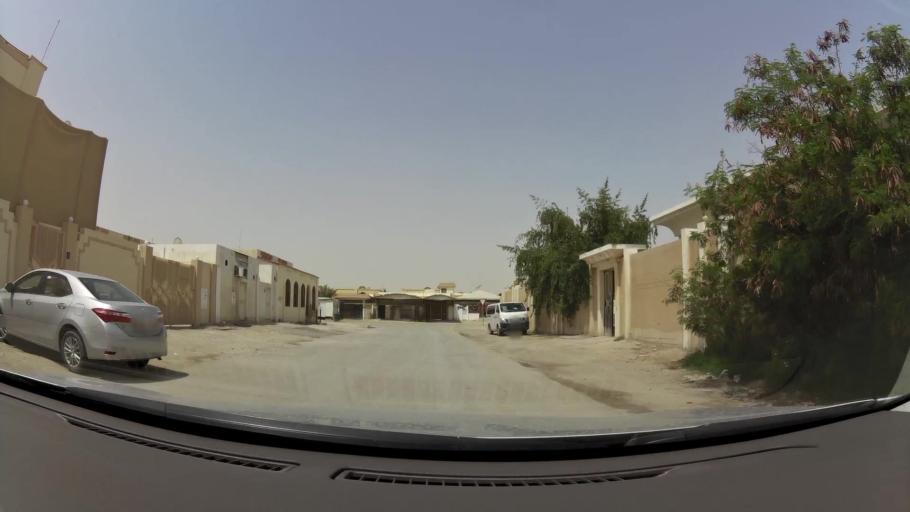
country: QA
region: Baladiyat ar Rayyan
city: Ar Rayyan
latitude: 25.2310
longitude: 51.4163
